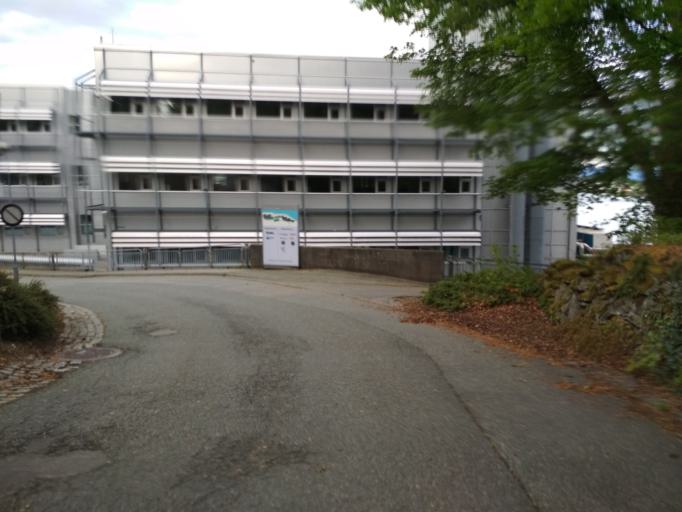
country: NO
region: Rogaland
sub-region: Stavanger
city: Stavanger
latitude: 58.9786
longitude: 5.7197
